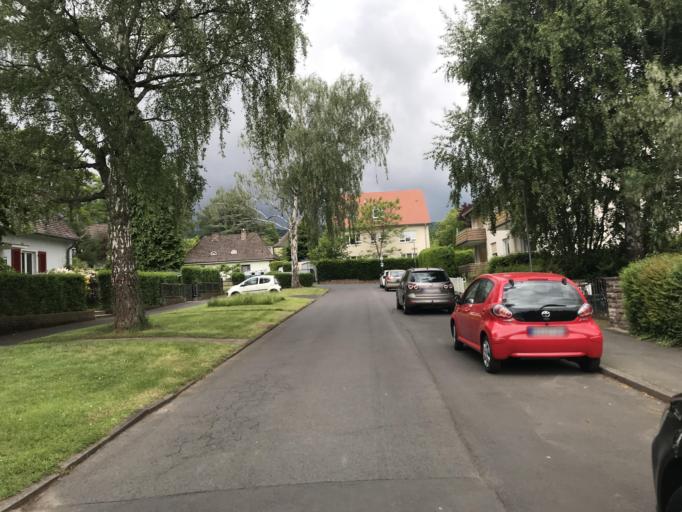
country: DE
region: Hesse
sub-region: Regierungsbezirk Kassel
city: Fuldabruck
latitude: 51.3097
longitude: 9.4370
